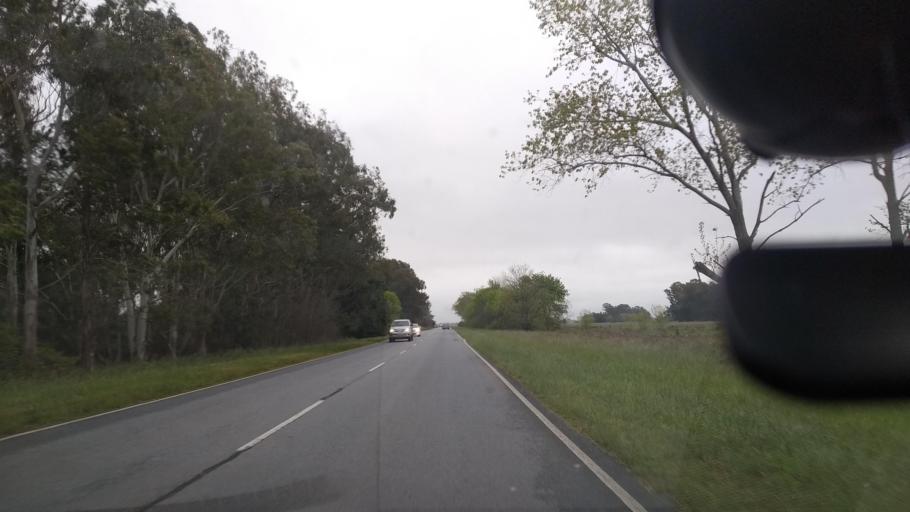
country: AR
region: Buenos Aires
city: Veronica
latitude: -35.3516
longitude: -57.4239
